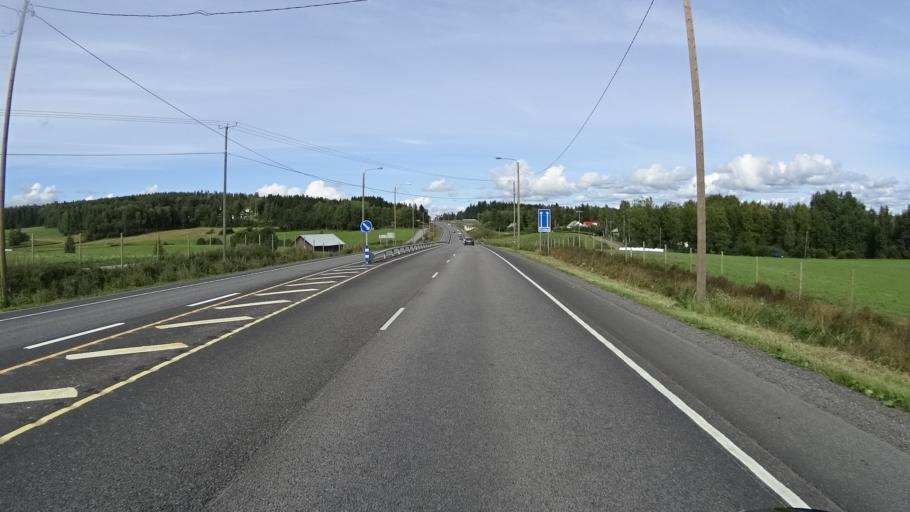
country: FI
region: Pirkanmaa
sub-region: Tampere
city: Haemeenkyroe
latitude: 61.6839
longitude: 23.1613
